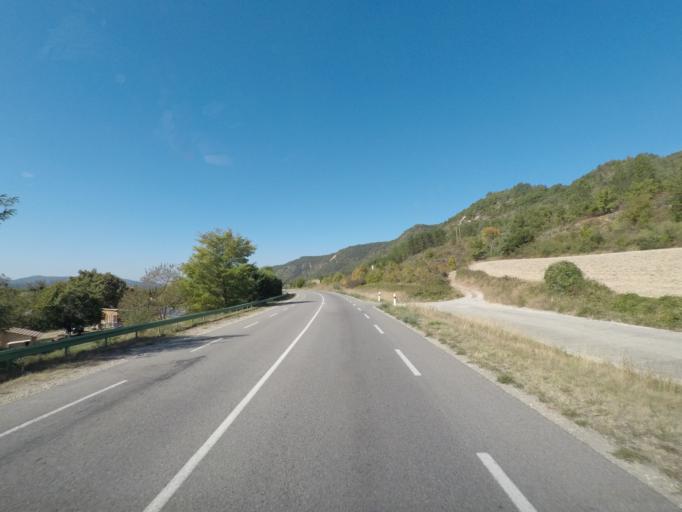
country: FR
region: Rhone-Alpes
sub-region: Departement de la Drome
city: Aouste-sur-Sye
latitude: 44.6961
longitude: 5.1657
